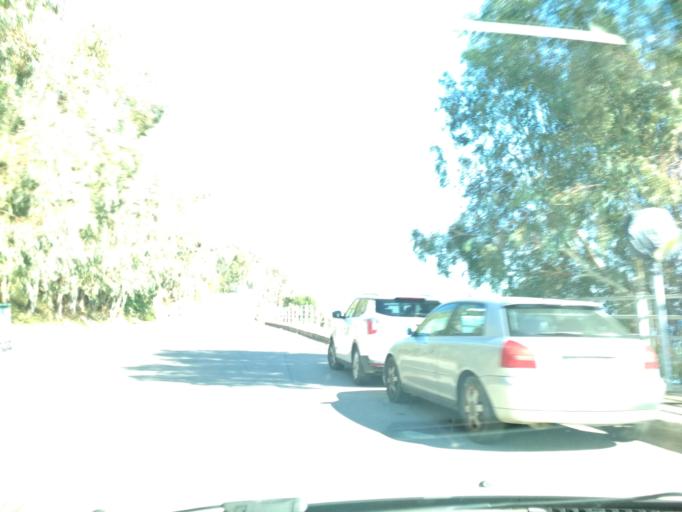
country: GR
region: Central Greece
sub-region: Nomos Evvoias
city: Oreoi
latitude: 38.8530
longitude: 23.0528
